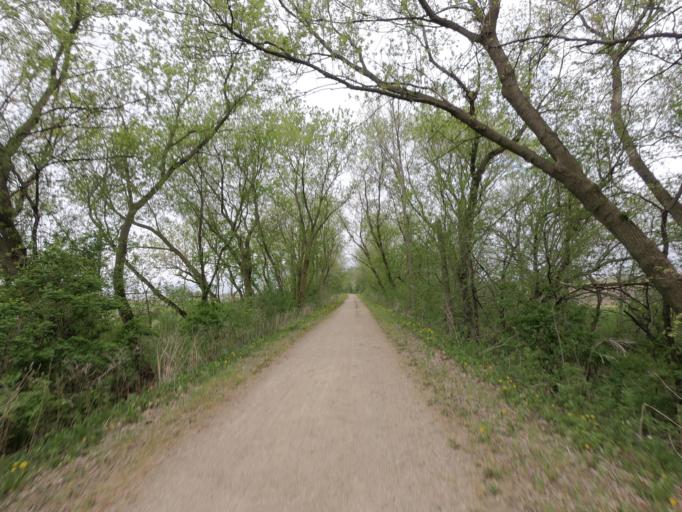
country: US
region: Wisconsin
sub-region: Jefferson County
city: Johnson Creek
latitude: 43.0372
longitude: -88.7662
